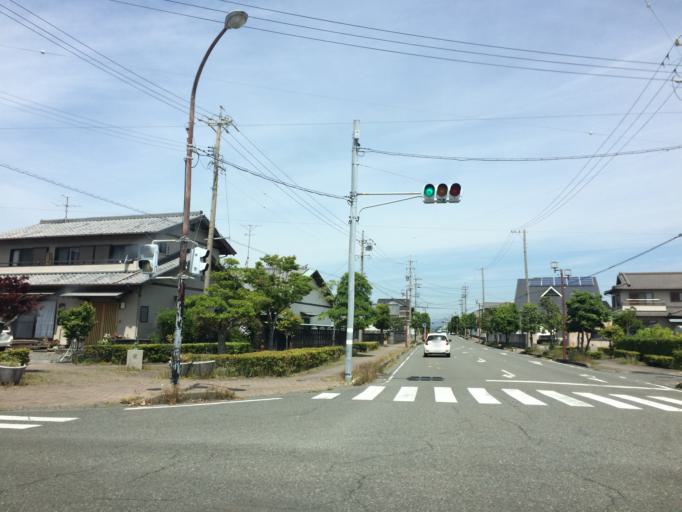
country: JP
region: Shizuoka
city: Sagara
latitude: 34.7549
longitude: 138.2536
